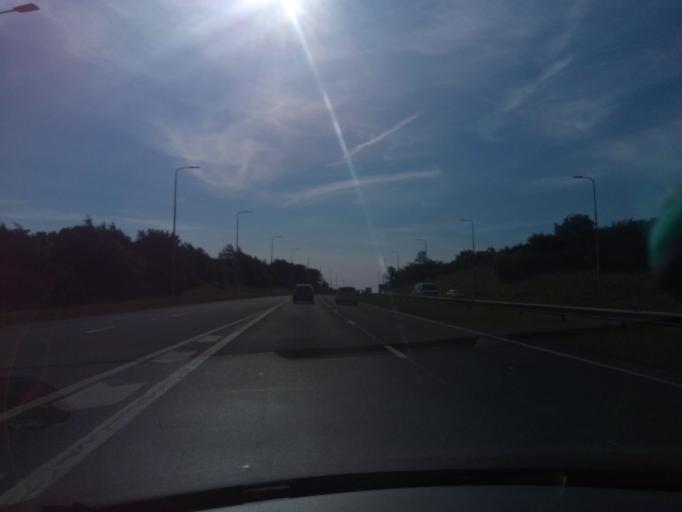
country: GB
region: England
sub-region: County Durham
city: Shotton
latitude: 54.7911
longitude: -1.3662
